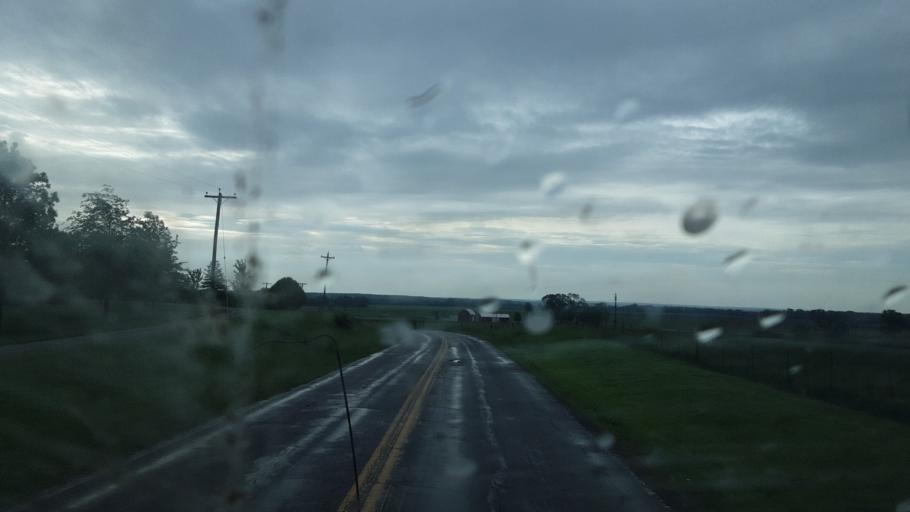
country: US
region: Missouri
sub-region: Clark County
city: Kahoka
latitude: 40.4311
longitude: -91.5812
